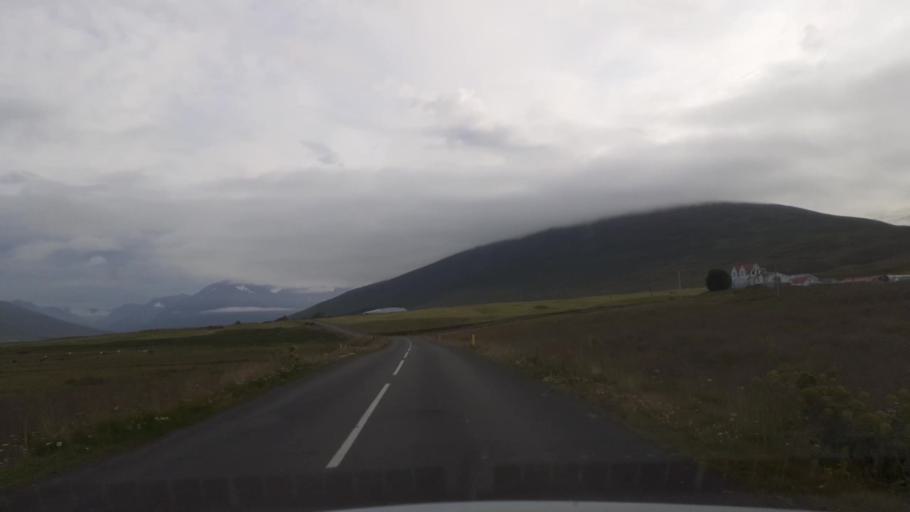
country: IS
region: Northeast
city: Dalvik
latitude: 65.9595
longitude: -18.5451
